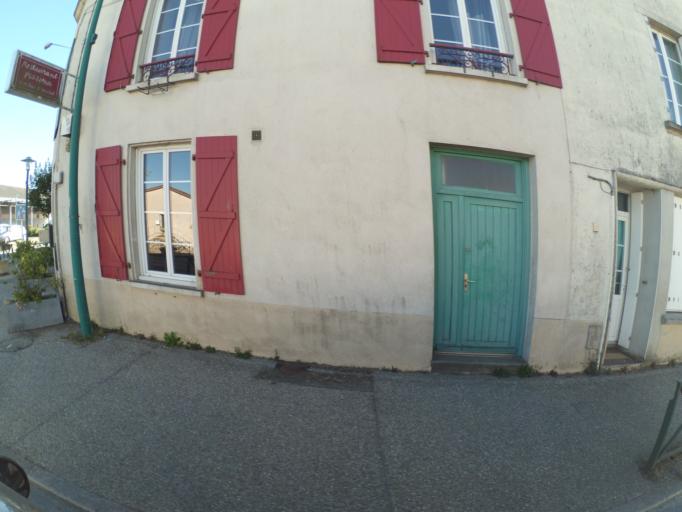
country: FR
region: Pays de la Loire
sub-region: Departement de la Vendee
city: Saint-Michel-Mont-Mercure
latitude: 46.8298
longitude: -0.8840
